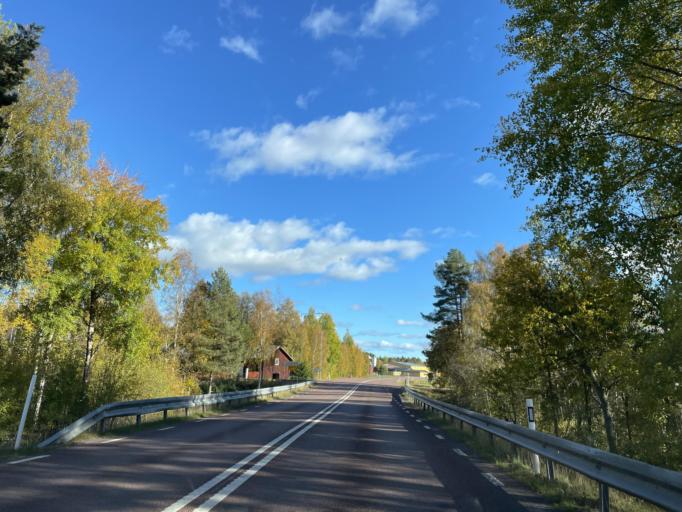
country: SE
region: Dalarna
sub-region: Malung-Saelens kommun
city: Malung
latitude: 60.7018
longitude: 13.6885
